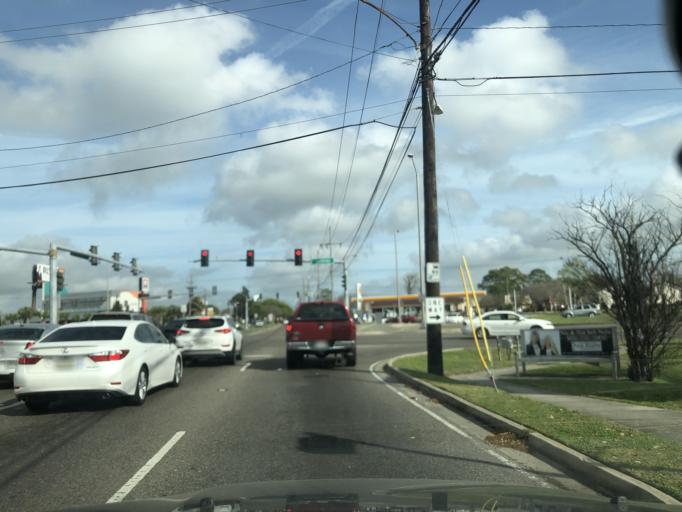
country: US
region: Louisiana
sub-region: Jefferson Parish
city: Metairie Terrace
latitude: 30.0052
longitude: -90.1947
